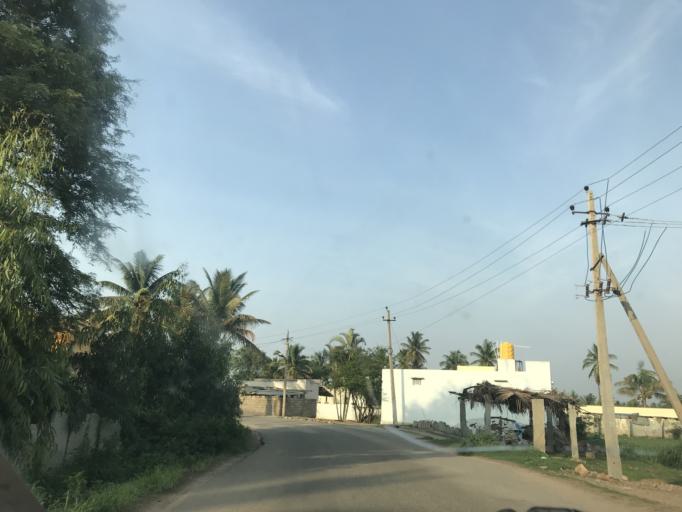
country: IN
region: Karnataka
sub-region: Bangalore Rural
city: Devanhalli
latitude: 13.2227
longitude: 77.6541
